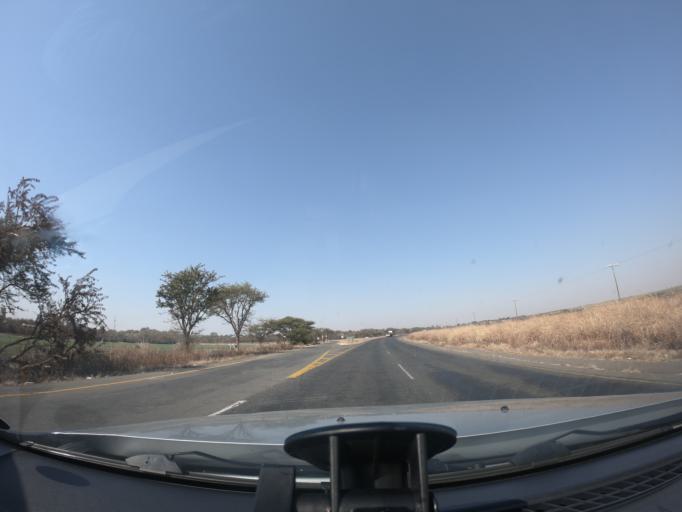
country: ZA
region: KwaZulu-Natal
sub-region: uThukela District Municipality
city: Ladysmith
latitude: -28.7356
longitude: 29.8160
